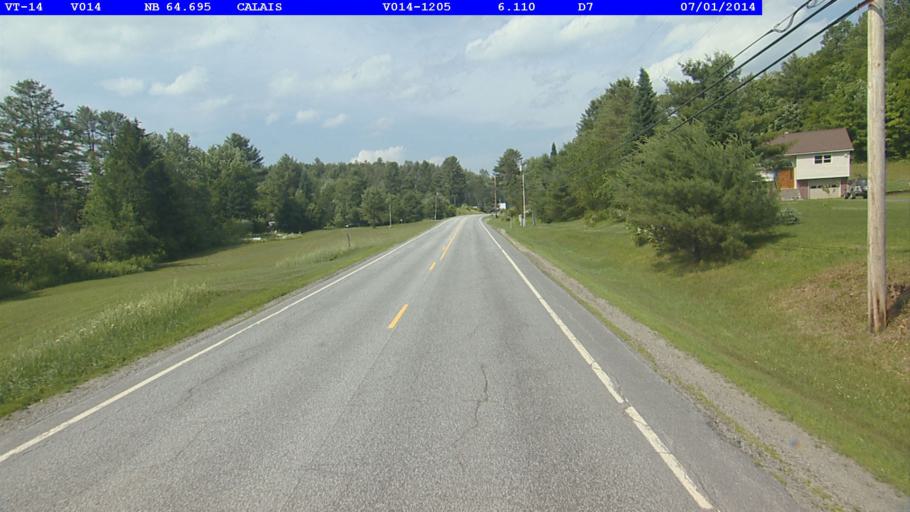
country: US
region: Vermont
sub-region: Caledonia County
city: Hardwick
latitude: 44.3852
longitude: -72.4175
